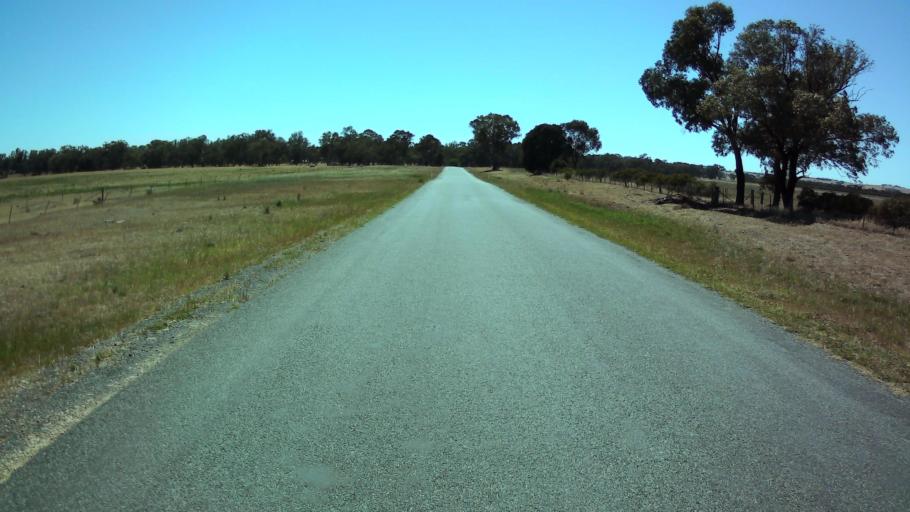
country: AU
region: New South Wales
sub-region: Weddin
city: Grenfell
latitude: -34.0015
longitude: 148.3883
